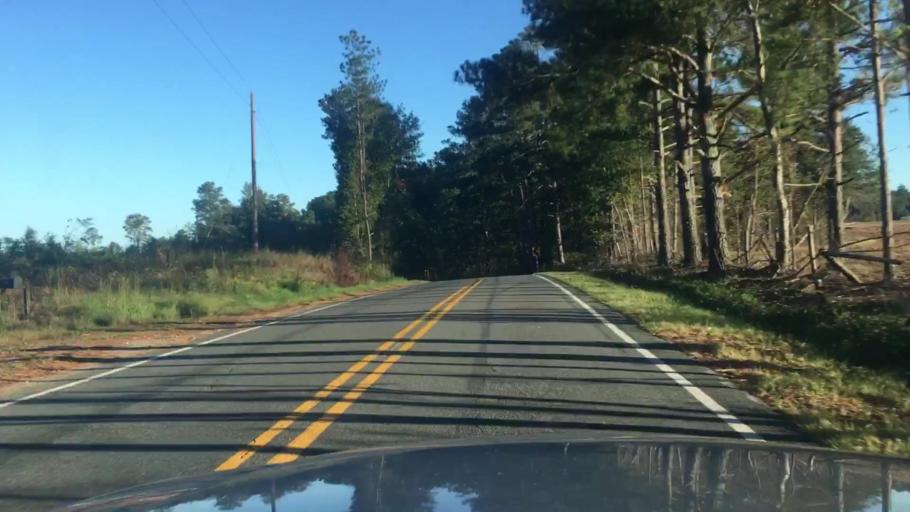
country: US
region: North Carolina
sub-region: Harnett County
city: Walkertown
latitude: 35.2871
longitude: -78.8693
